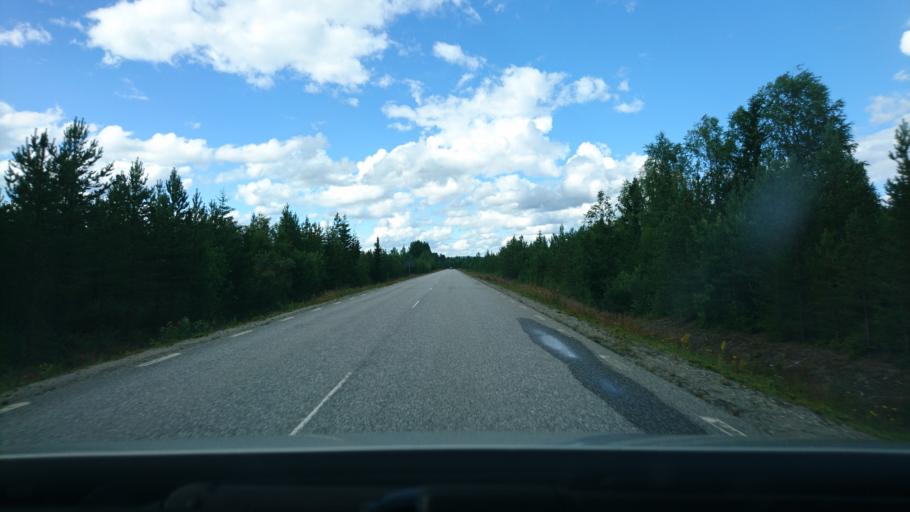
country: SE
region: Vaesterbotten
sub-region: Asele Kommun
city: Asele
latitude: 63.9633
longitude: 17.2671
